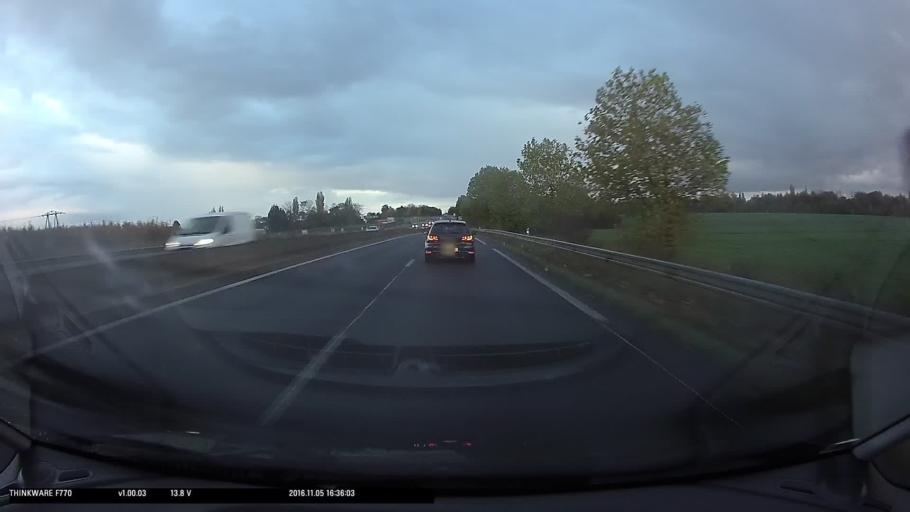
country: FR
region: Ile-de-France
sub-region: Departement du Val-d'Oise
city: Courdimanche
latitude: 49.0607
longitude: 1.9937
